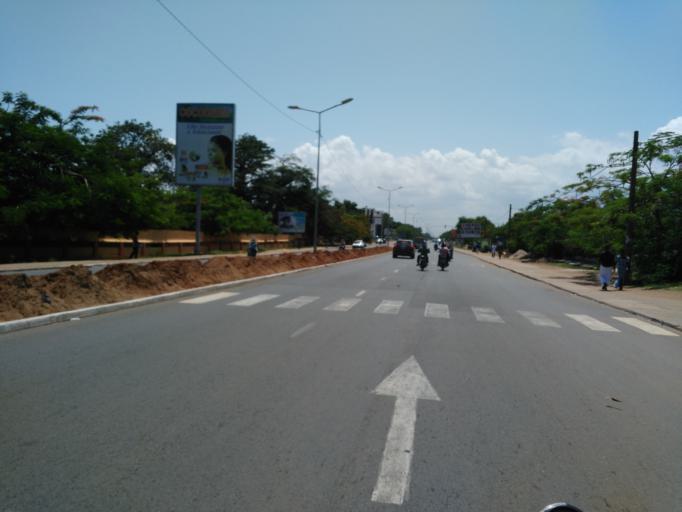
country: TG
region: Maritime
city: Lome
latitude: 6.1537
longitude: 1.2287
